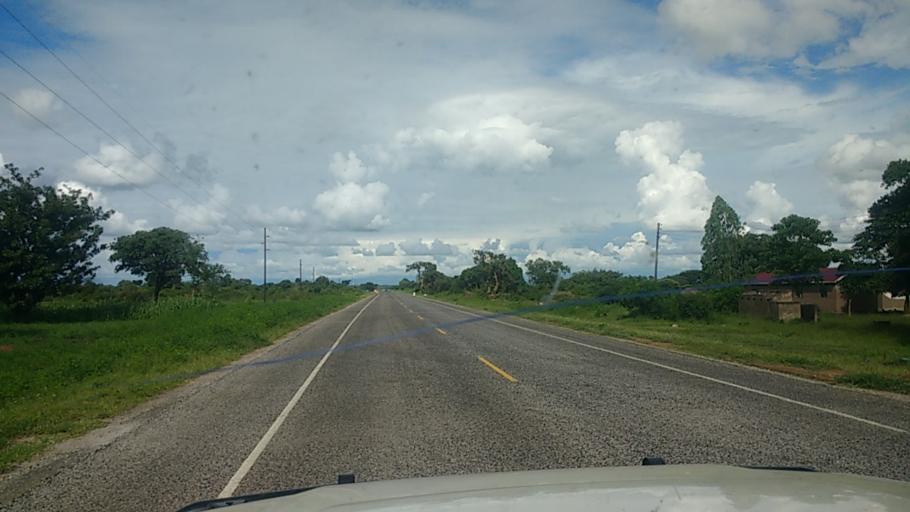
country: UG
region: Eastern Region
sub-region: Katakwi District
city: Katakwi
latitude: 1.9190
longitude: 34.0038
